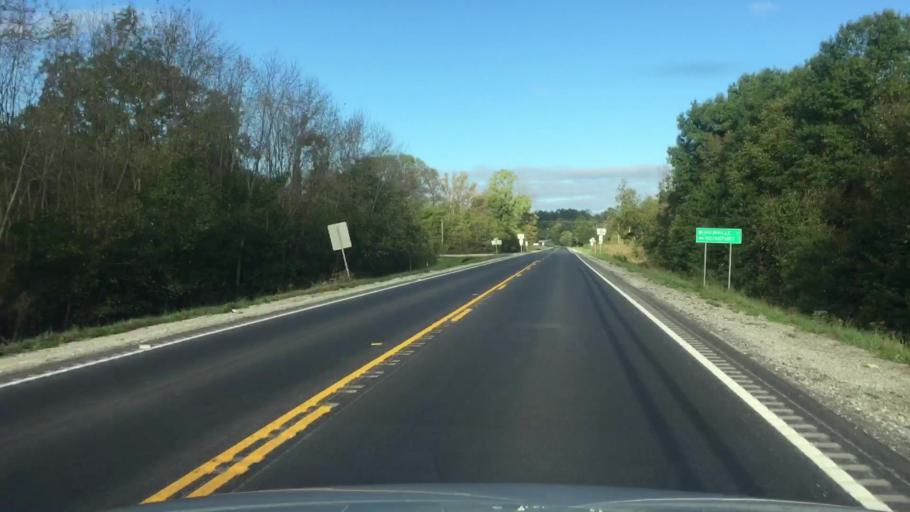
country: US
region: Missouri
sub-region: Howard County
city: New Franklin
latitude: 38.9943
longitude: -92.5686
